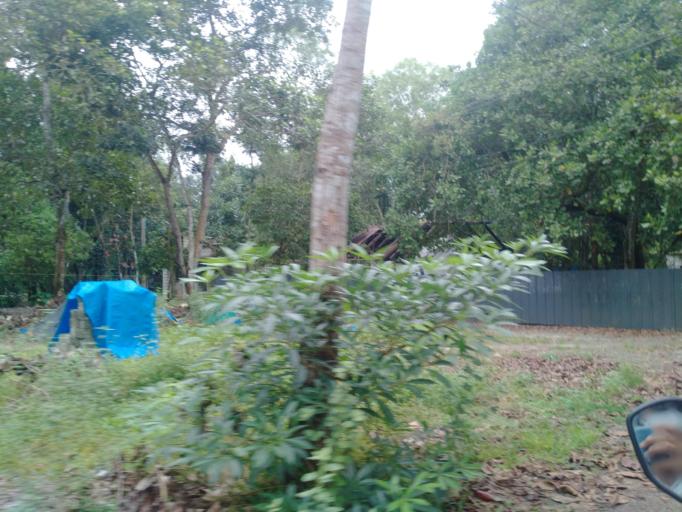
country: IN
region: Kerala
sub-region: Alappuzha
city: Shertallai
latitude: 9.6209
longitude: 76.3567
